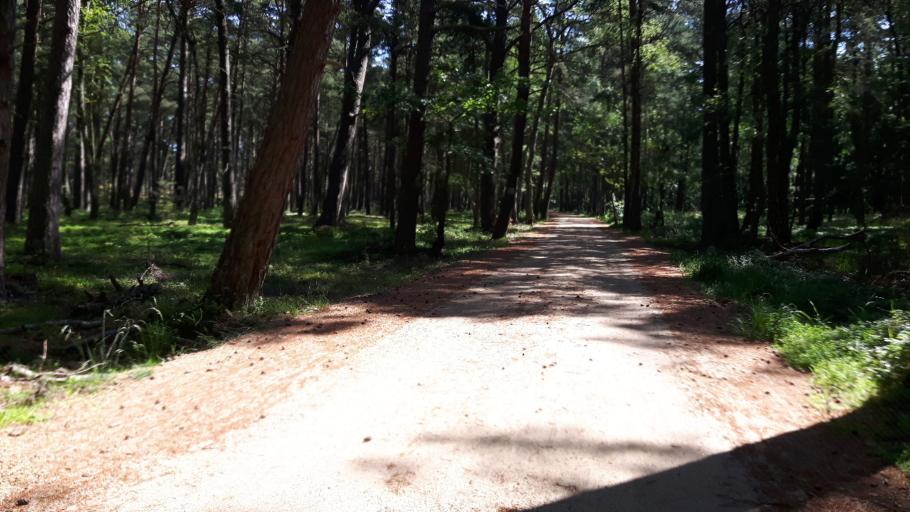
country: PL
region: Pomeranian Voivodeship
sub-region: Powiat slupski
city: Smoldzino
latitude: 54.6739
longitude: 17.1143
